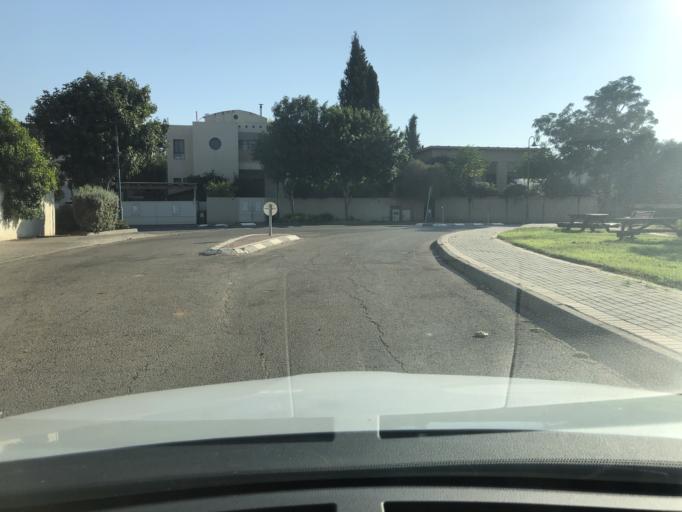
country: IL
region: Central District
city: Hod HaSharon
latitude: 32.1394
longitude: 34.9093
